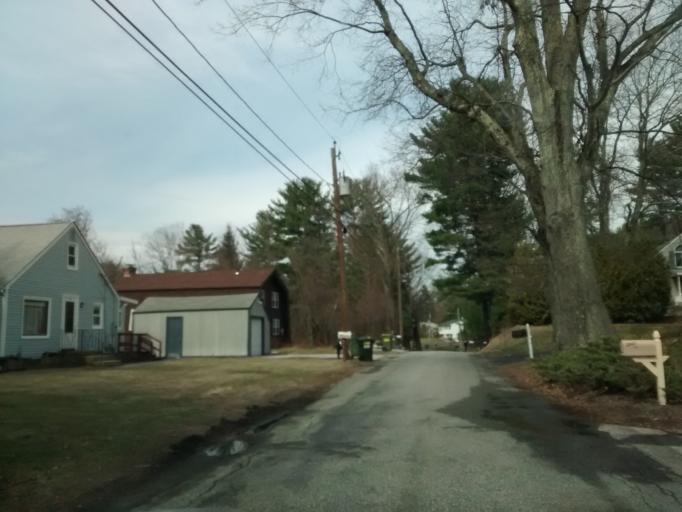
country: US
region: Massachusetts
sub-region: Worcester County
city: Oxford
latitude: 42.1145
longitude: -71.8749
